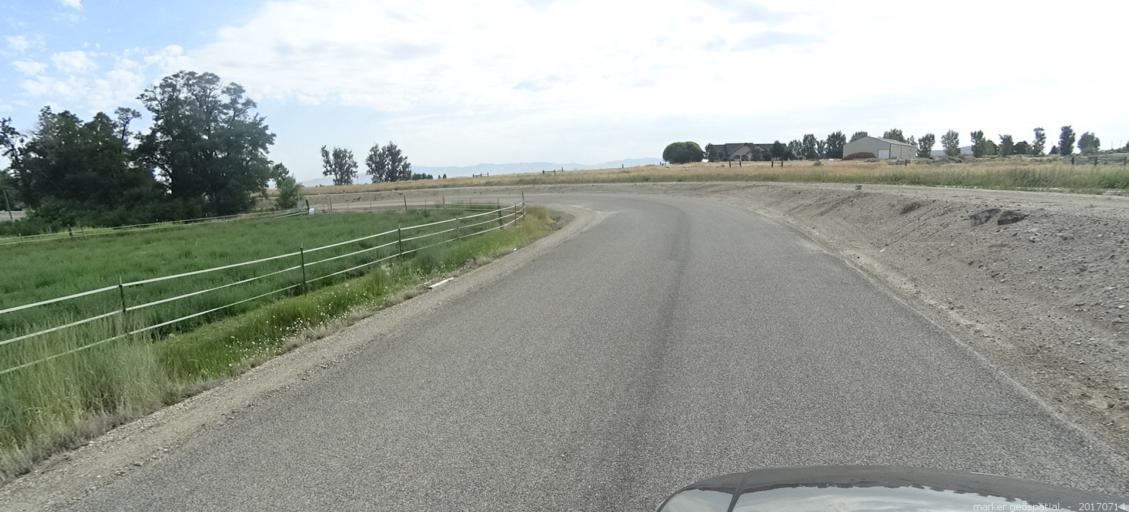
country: US
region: Idaho
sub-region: Ada County
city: Kuna
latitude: 43.4597
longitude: -116.3752
